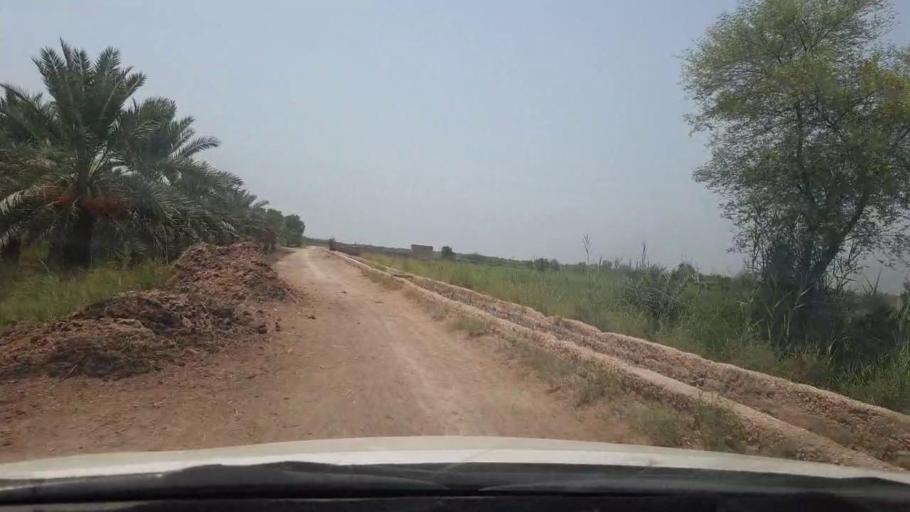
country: PK
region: Sindh
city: Khairpur
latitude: 27.5107
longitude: 68.8120
